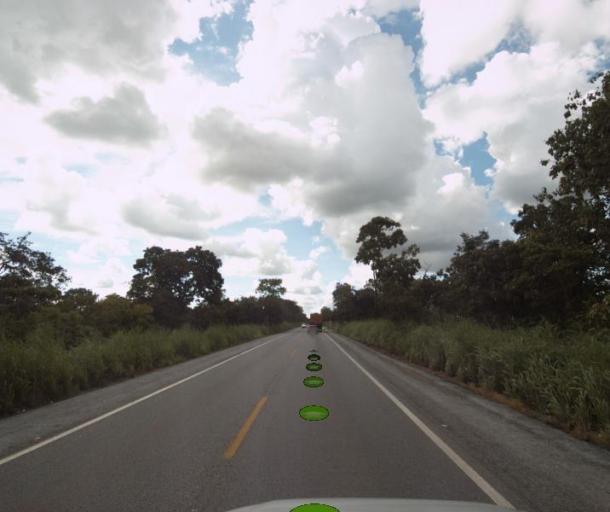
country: BR
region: Goias
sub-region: Porangatu
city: Porangatu
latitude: -13.1824
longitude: -49.1671
